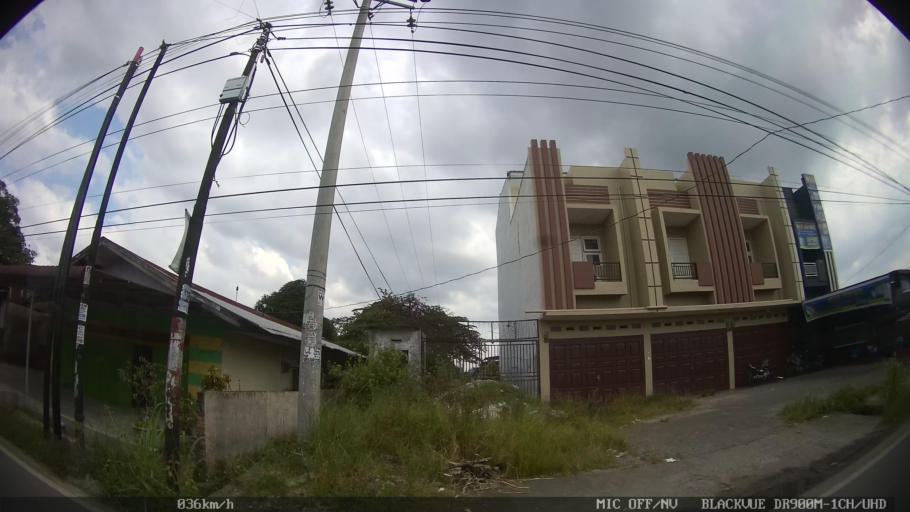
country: ID
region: North Sumatra
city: Sunggal
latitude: 3.6186
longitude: 98.6061
